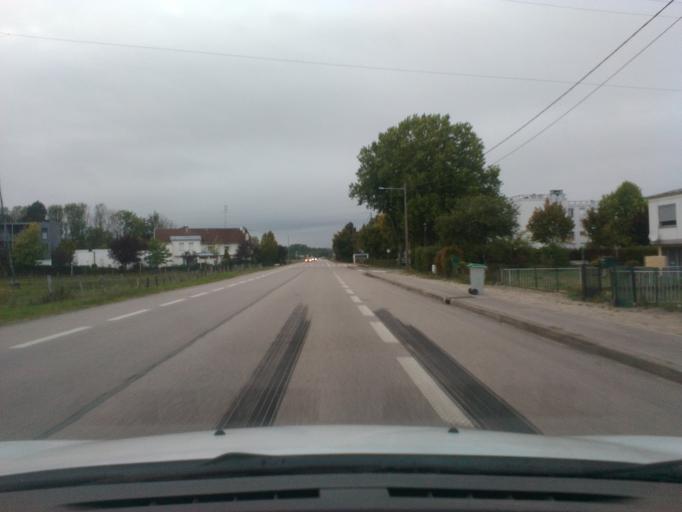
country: FR
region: Lorraine
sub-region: Departement des Vosges
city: Vincey
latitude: 48.3484
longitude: 6.3222
